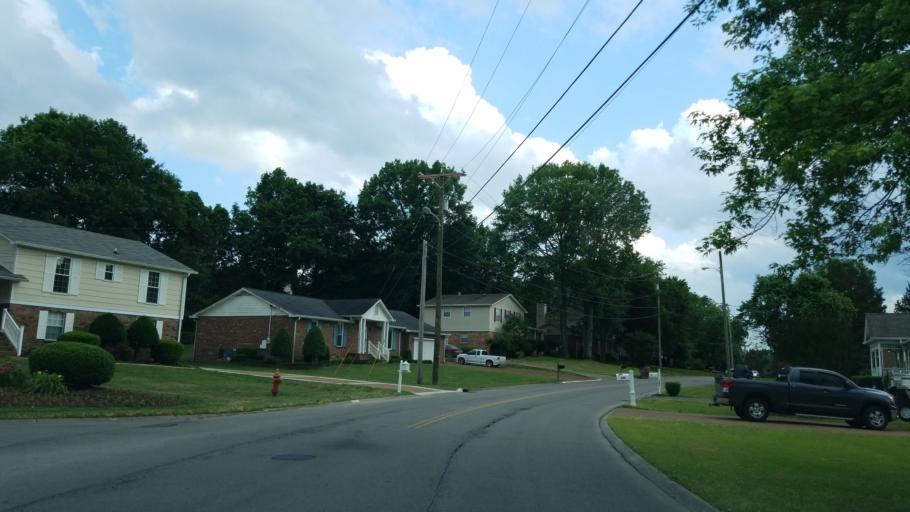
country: US
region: Tennessee
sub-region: Rutherford County
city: La Vergne
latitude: 36.0930
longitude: -86.6139
